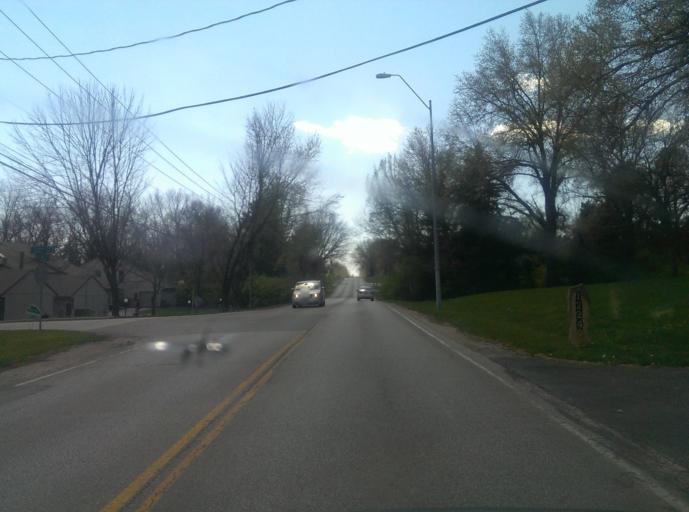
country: US
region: Missouri
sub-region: Jackson County
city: Grandview
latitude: 38.9051
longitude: -94.5849
